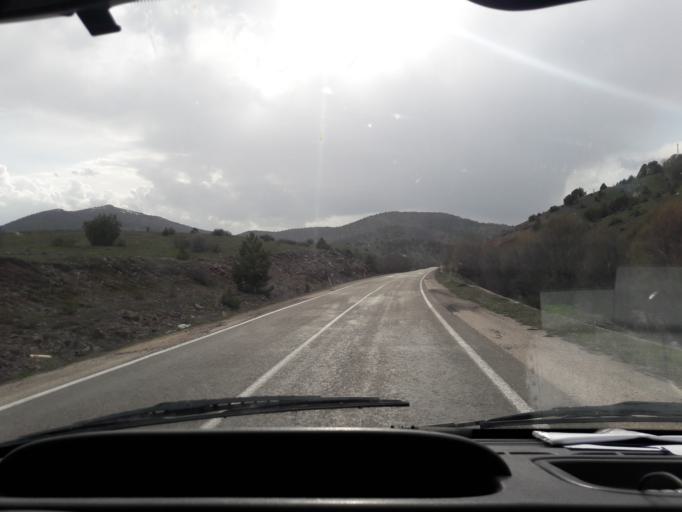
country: TR
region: Giresun
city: Alucra
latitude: 40.2645
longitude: 38.8995
